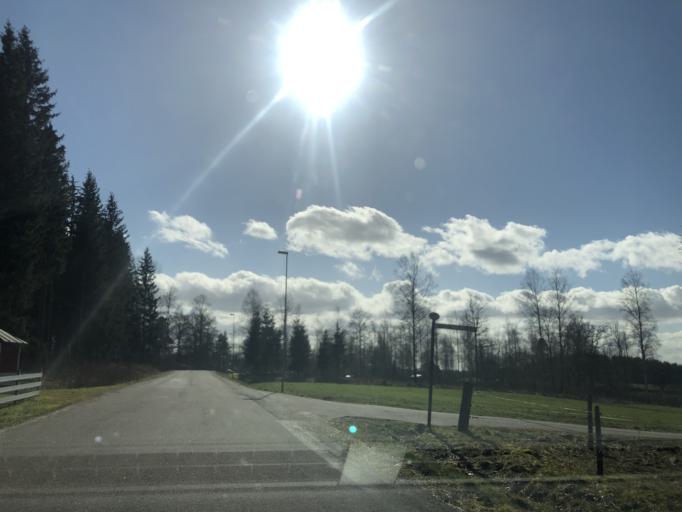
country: SE
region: Vaestra Goetaland
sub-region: Ulricehamns Kommun
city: Ulricehamn
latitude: 57.6904
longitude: 13.4185
